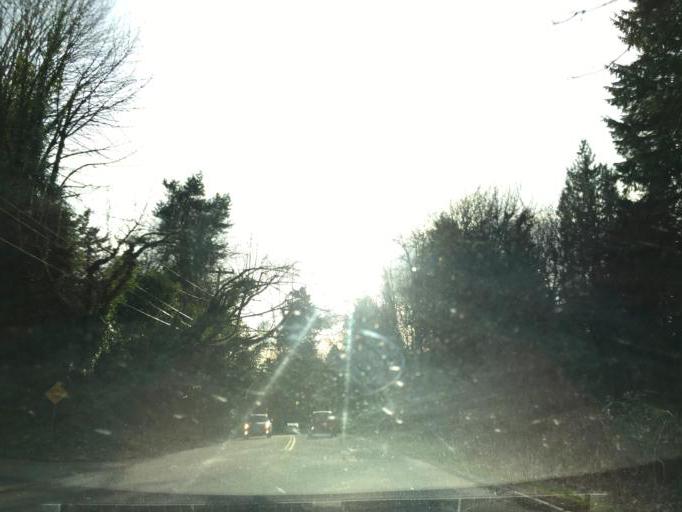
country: US
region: Oregon
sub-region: Clackamas County
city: Lake Oswego
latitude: 45.4519
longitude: -122.6832
